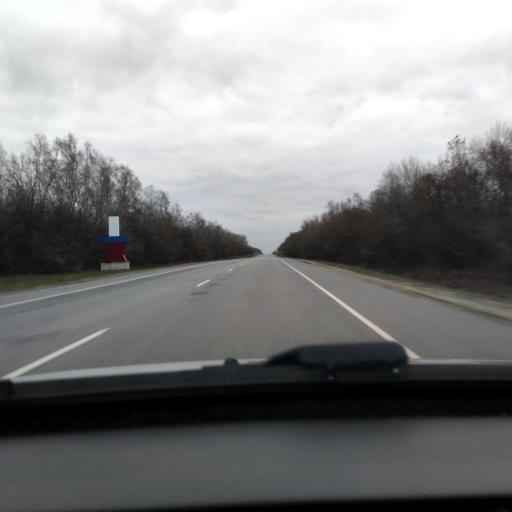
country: RU
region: Lipetsk
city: Khlevnoye
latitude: 52.3431
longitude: 39.1862
